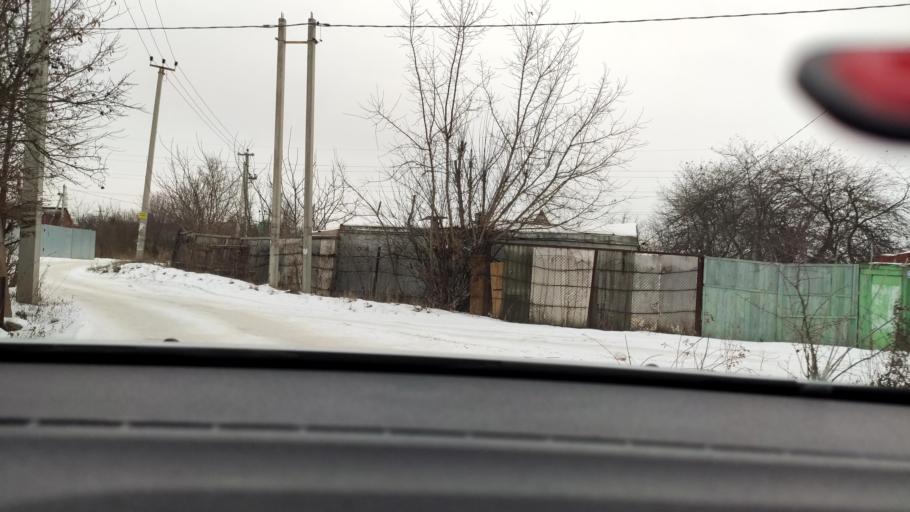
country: RU
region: Voronezj
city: Semiluki
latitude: 51.6975
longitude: 38.9936
